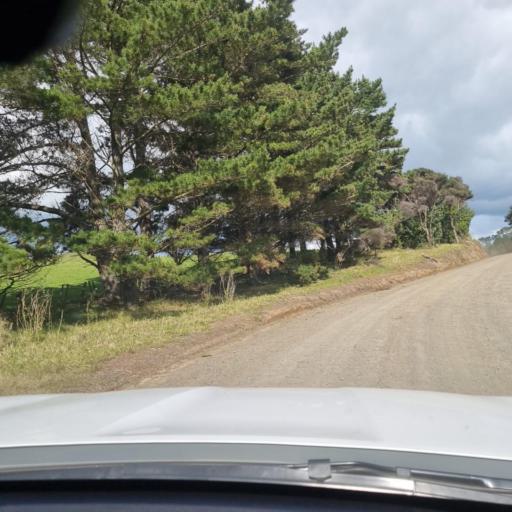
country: NZ
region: Auckland
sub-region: Auckland
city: Wellsford
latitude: -36.3400
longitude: 174.1624
